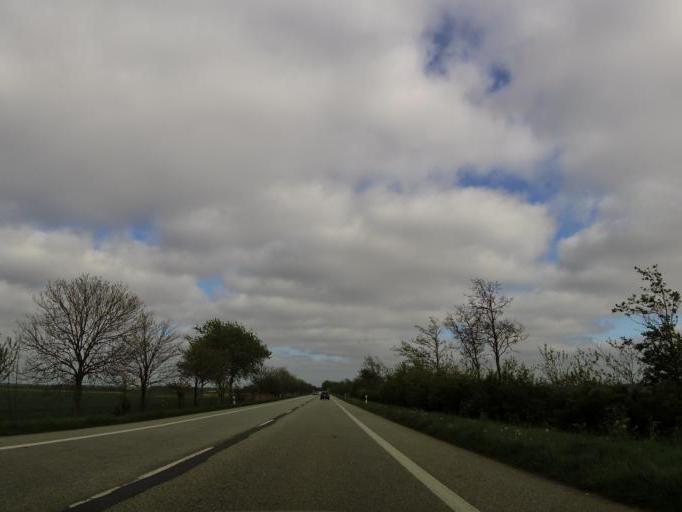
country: DE
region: Schleswig-Holstein
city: Risum-Lindholm
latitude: 54.7566
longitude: 8.8880
